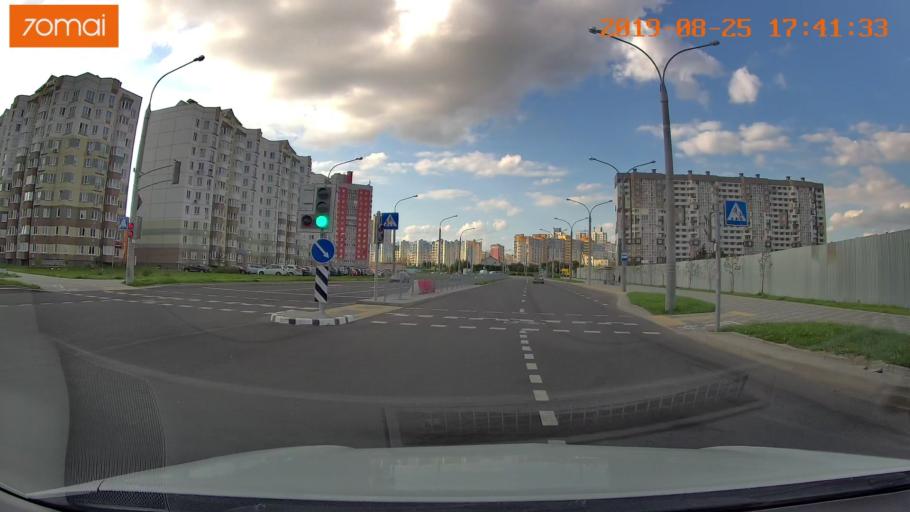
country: BY
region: Minsk
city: Novoye Medvezhino
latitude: 53.8725
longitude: 27.4565
